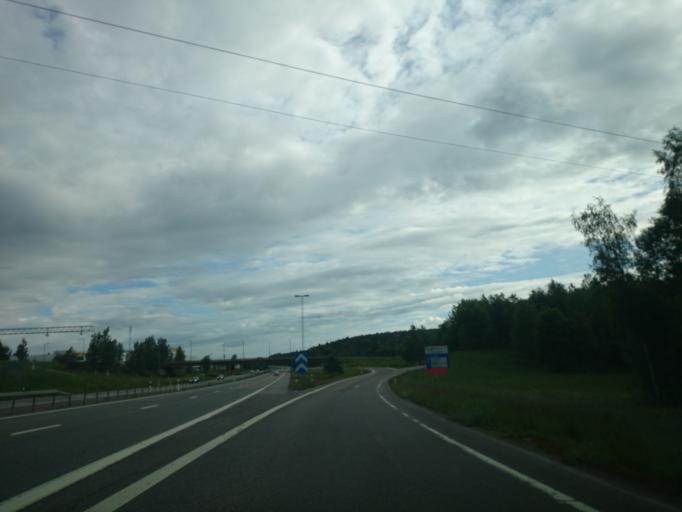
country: SE
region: Vaesternorrland
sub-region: Sundsvalls Kommun
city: Sundsvall
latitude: 62.4101
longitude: 17.3390
